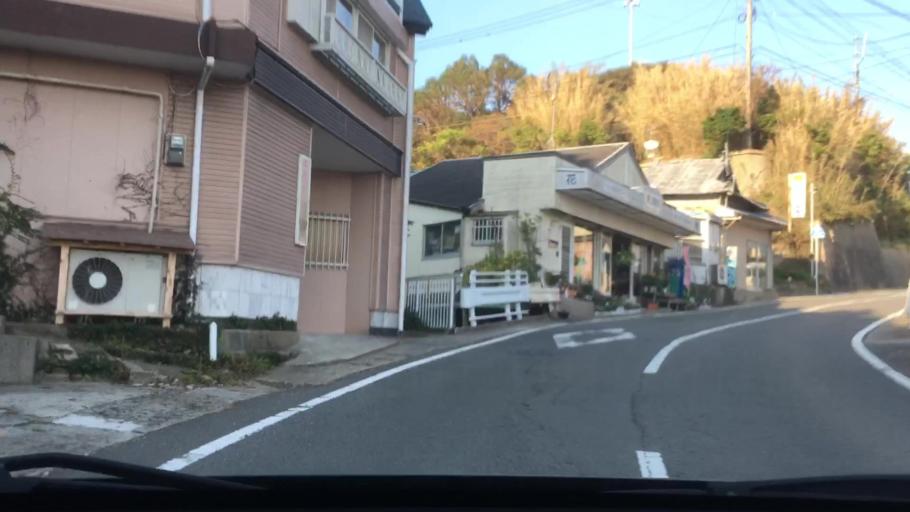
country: JP
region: Nagasaki
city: Sasebo
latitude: 33.0379
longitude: 129.6194
